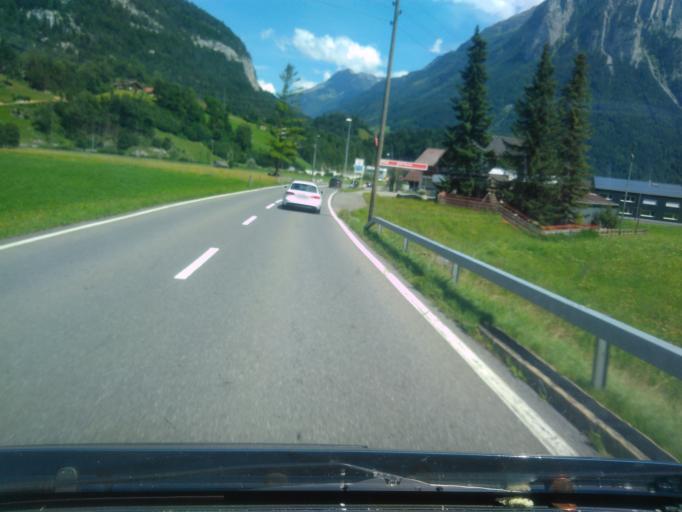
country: CH
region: Bern
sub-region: Interlaken-Oberhasli District
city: Meiringen
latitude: 46.7085
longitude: 8.2161
